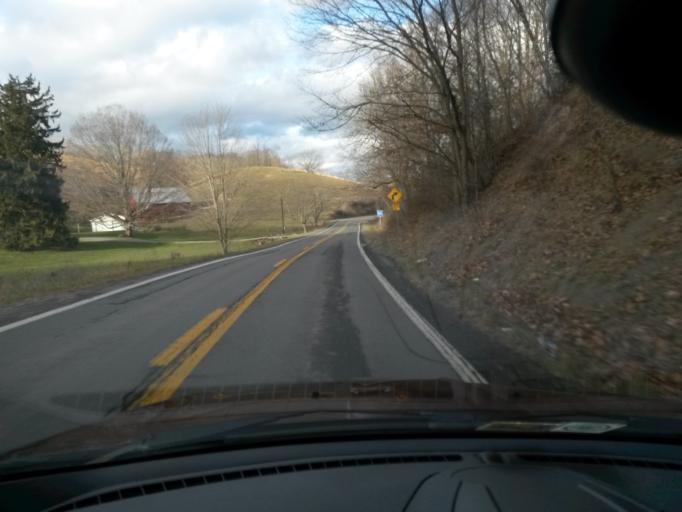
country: US
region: Virginia
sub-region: Giles County
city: Pembroke
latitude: 37.4657
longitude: -80.6604
